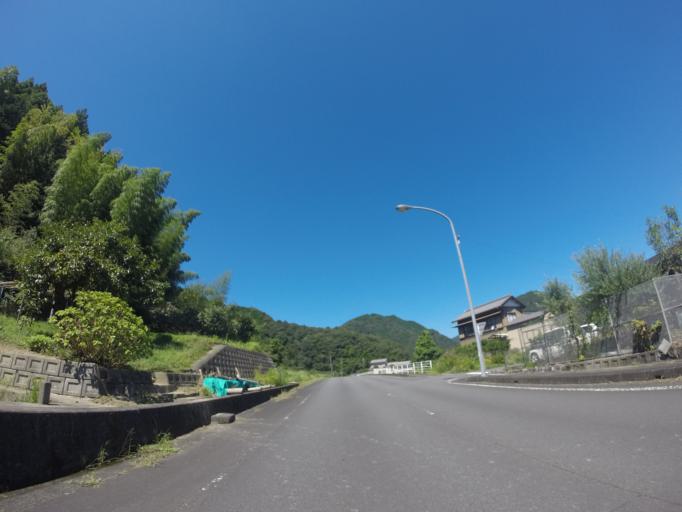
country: JP
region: Shizuoka
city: Fujieda
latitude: 34.9107
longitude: 138.1925
